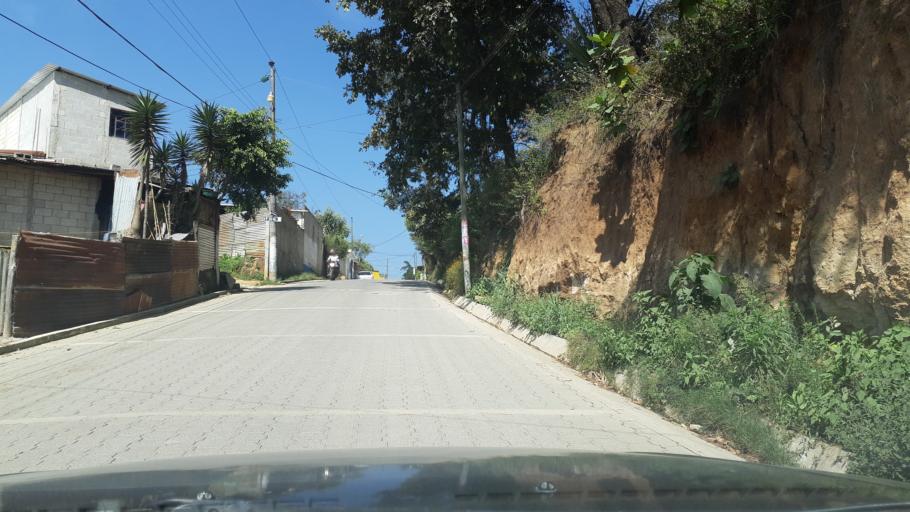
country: GT
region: Chimaltenango
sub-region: Municipio de Chimaltenango
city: Chimaltenango
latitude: 14.6718
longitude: -90.8400
